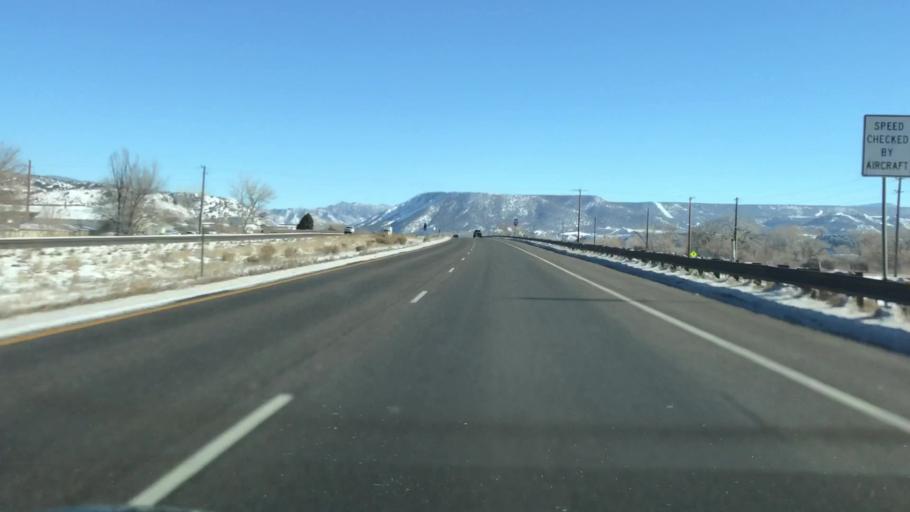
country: US
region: Colorado
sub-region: Garfield County
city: Silt
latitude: 39.5442
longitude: -107.6475
